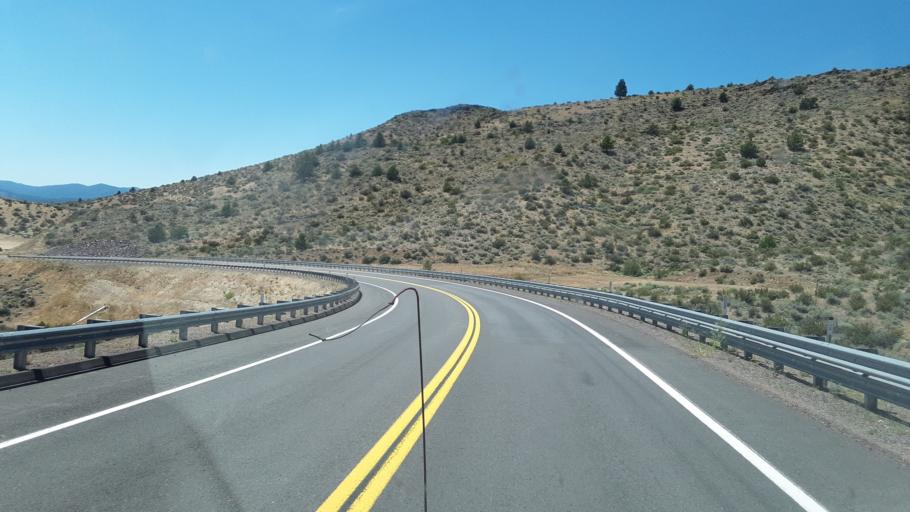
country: US
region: California
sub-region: Lassen County
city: Johnstonville
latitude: 40.4633
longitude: -120.5749
